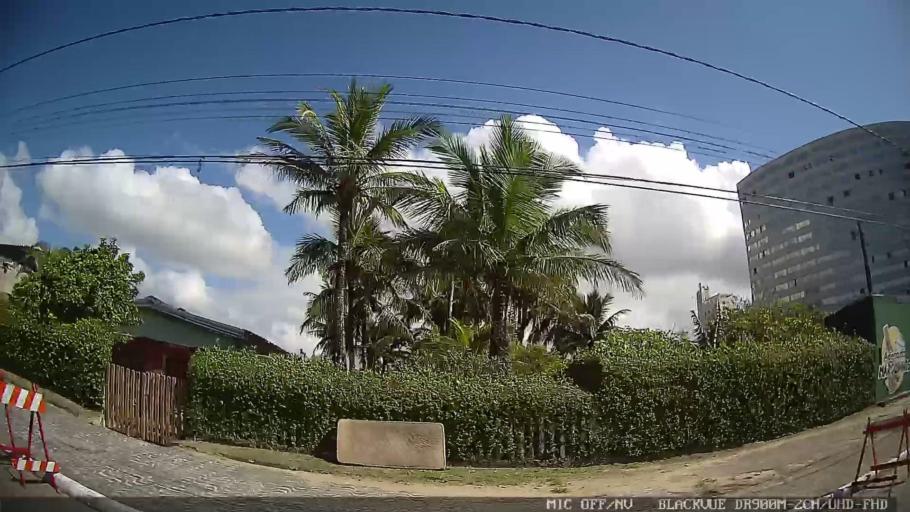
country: BR
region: Sao Paulo
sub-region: Peruibe
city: Peruibe
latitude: -24.3262
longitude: -46.9967
